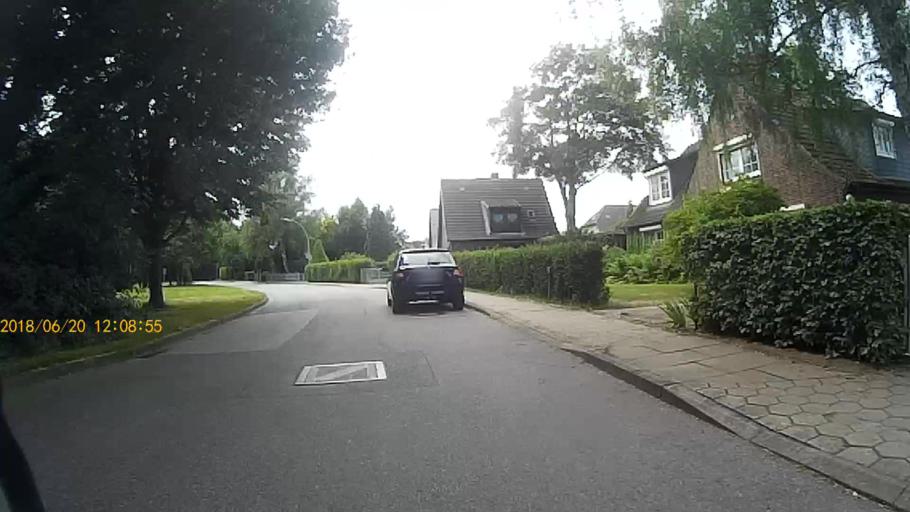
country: DE
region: Hamburg
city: Harburg
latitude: 53.4833
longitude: 10.0076
